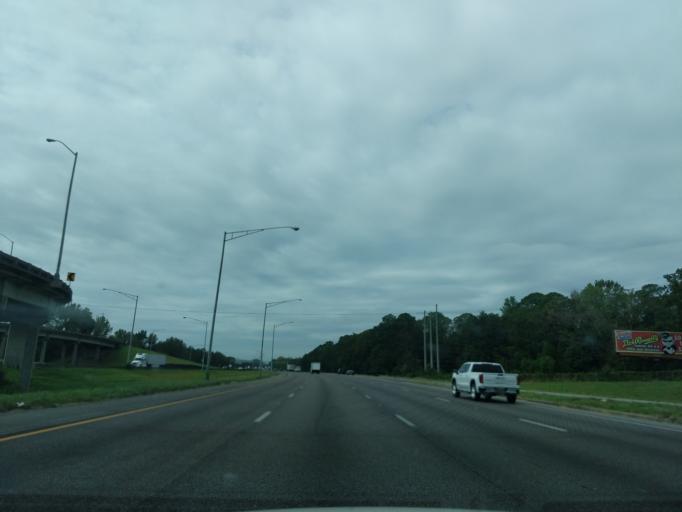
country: US
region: Alabama
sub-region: Mobile County
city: Mobile
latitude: 30.6405
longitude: -88.0913
